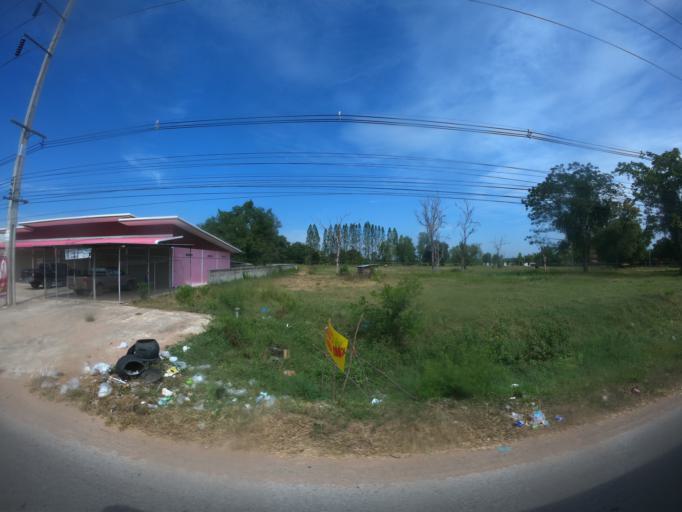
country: TH
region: Maha Sarakham
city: Chiang Yuen
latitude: 16.4443
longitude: 103.0095
